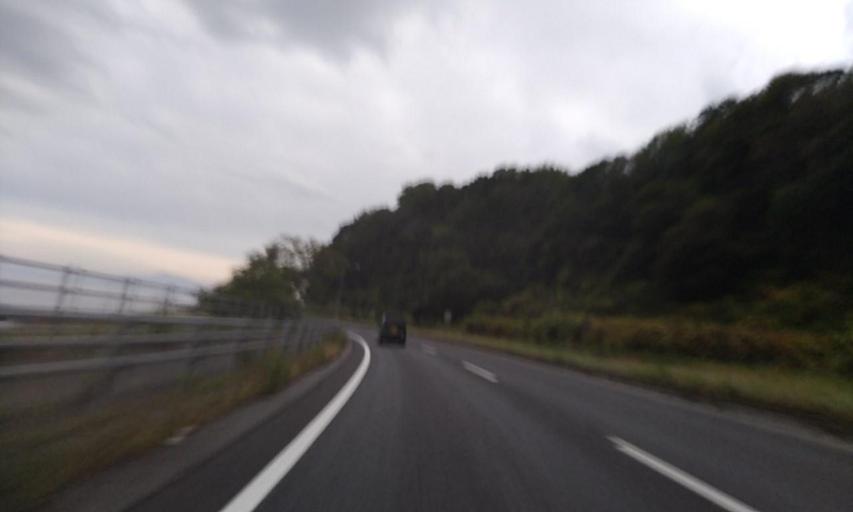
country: JP
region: Hokkaido
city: Abashiri
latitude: 44.0035
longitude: 144.2869
